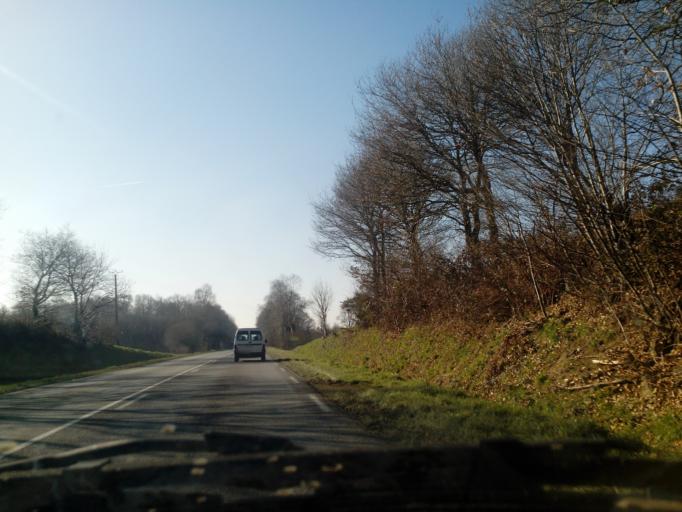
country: FR
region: Brittany
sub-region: Departement des Cotes-d'Armor
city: Plemet
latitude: 48.1792
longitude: -2.5562
